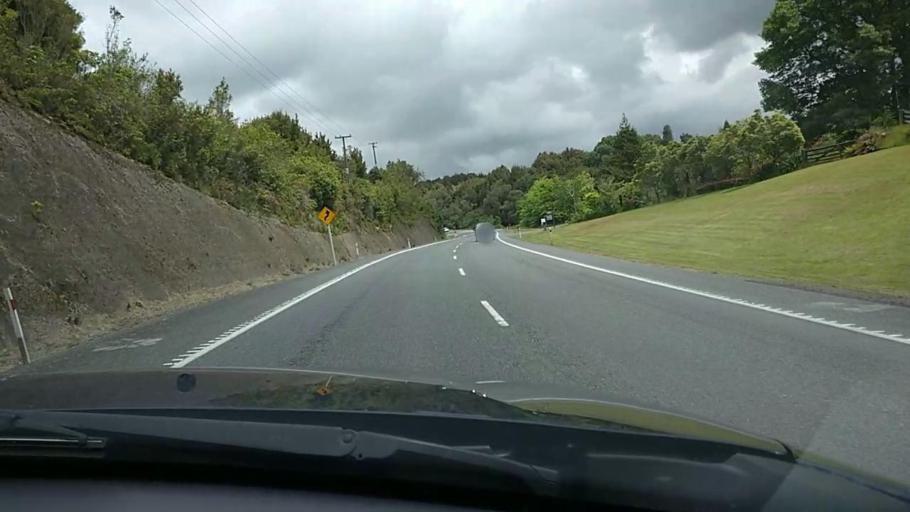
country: NZ
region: Bay of Plenty
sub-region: Rotorua District
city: Rotorua
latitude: -38.0715
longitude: 176.1213
